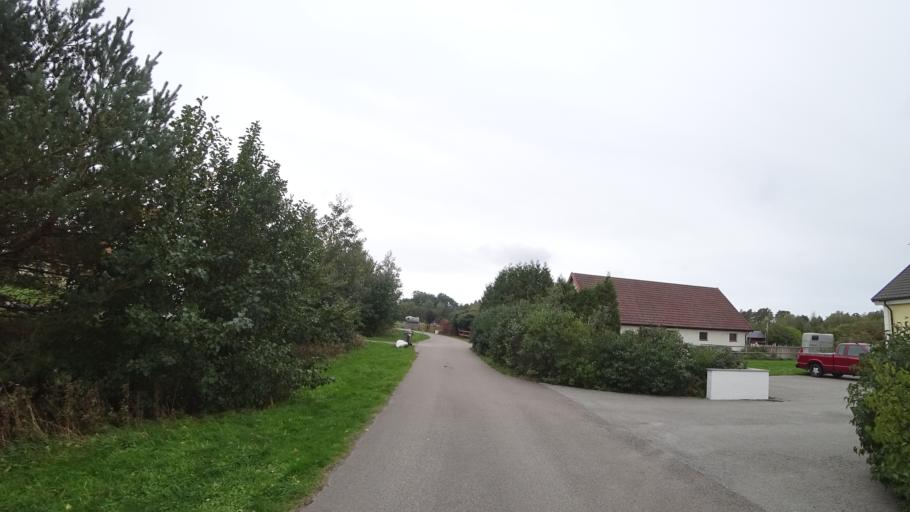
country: SE
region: Skane
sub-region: Kavlinge Kommun
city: Hofterup
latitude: 55.7991
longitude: 12.9953
